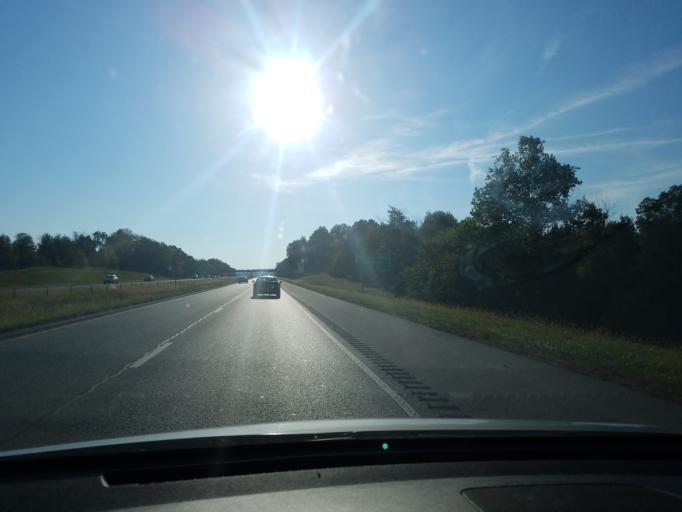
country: US
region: Indiana
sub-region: Floyd County
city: New Albany
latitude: 38.3419
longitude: -85.8064
